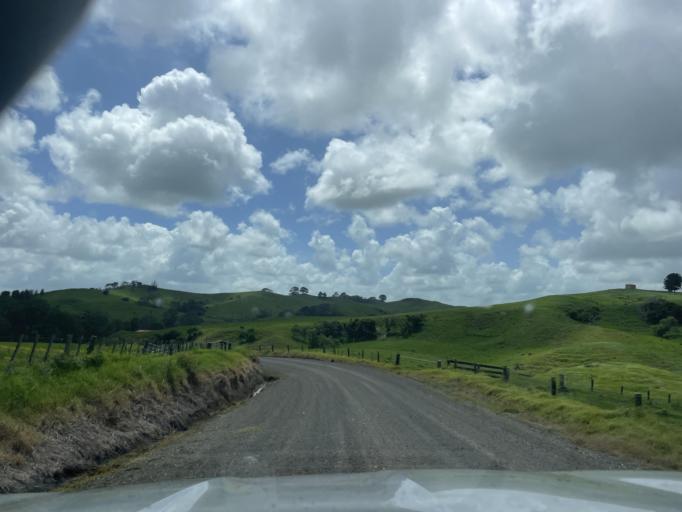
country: NZ
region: Auckland
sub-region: Auckland
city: Wellsford
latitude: -36.1948
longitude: 174.3351
